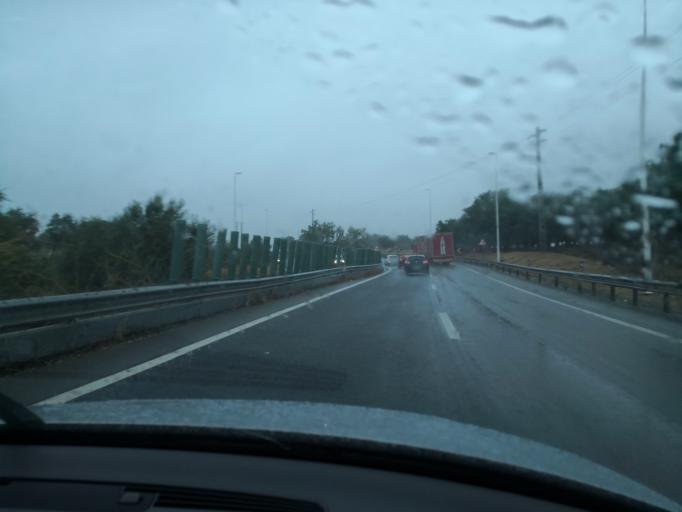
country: PT
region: Setubal
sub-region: Montijo
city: Montijo
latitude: 38.7119
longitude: -8.9389
